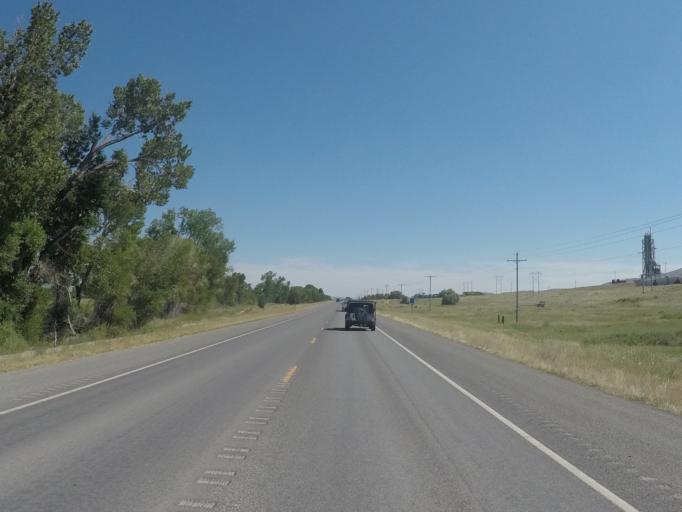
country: US
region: Montana
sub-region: Broadwater County
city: Townsend
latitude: 46.3409
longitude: -111.5346
